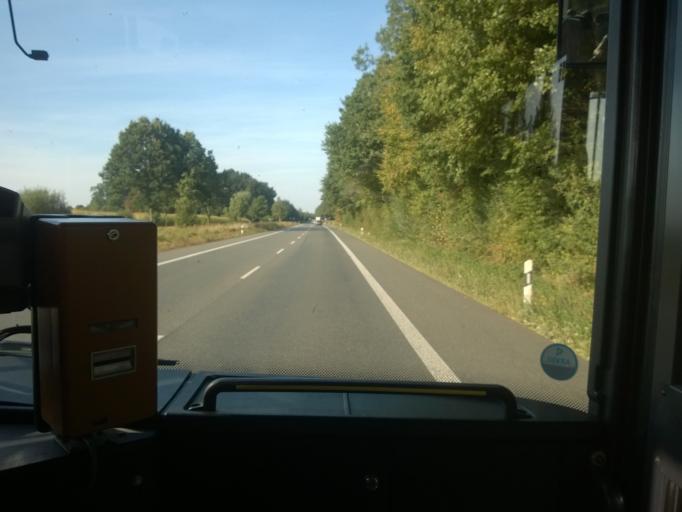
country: DE
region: North Rhine-Westphalia
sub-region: Regierungsbezirk Munster
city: Borken
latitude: 51.8872
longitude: 6.8579
